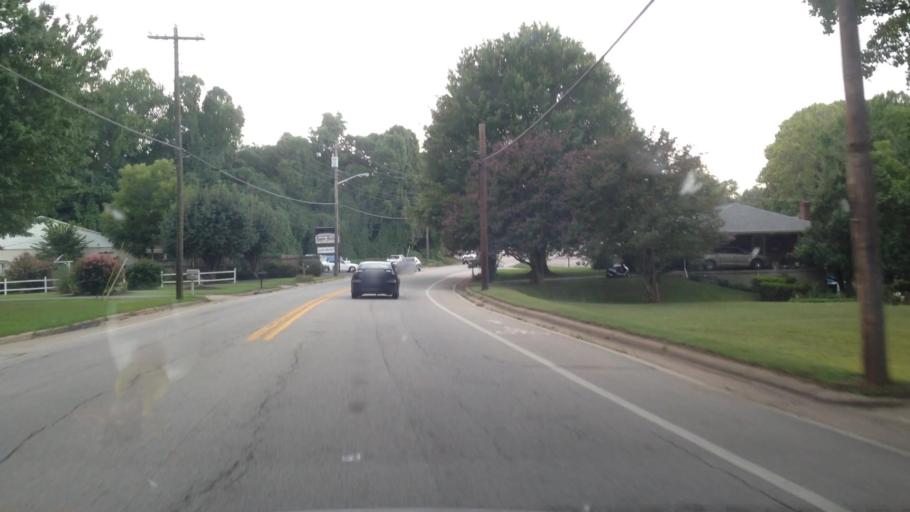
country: US
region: Virginia
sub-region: City of Danville
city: Danville
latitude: 36.5859
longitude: -79.4370
